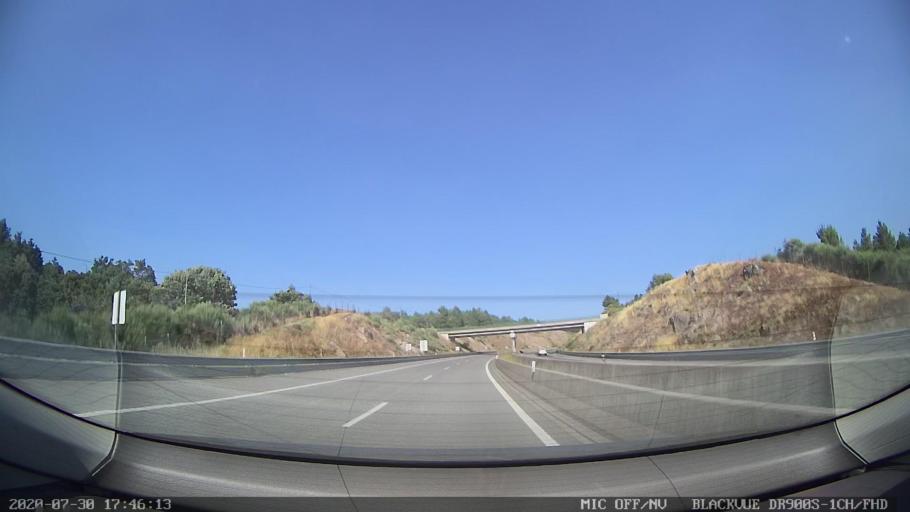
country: PT
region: Vila Real
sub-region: Sabrosa
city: Sabrosa
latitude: 41.3603
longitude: -7.5901
